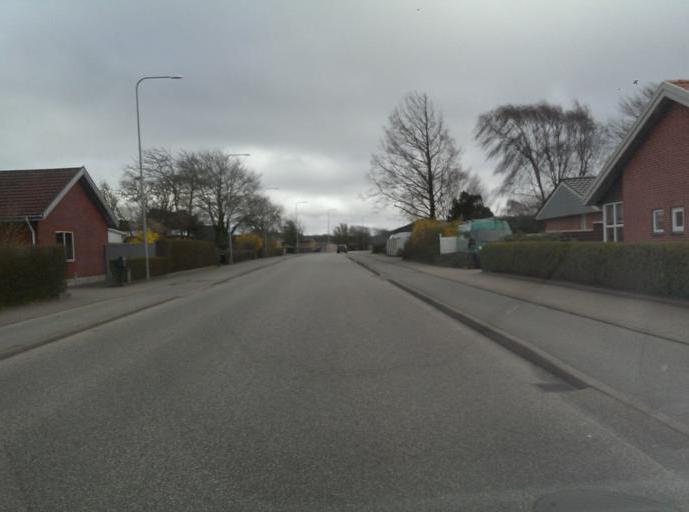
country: DK
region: South Denmark
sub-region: Esbjerg Kommune
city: Esbjerg
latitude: 55.4848
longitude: 8.4775
